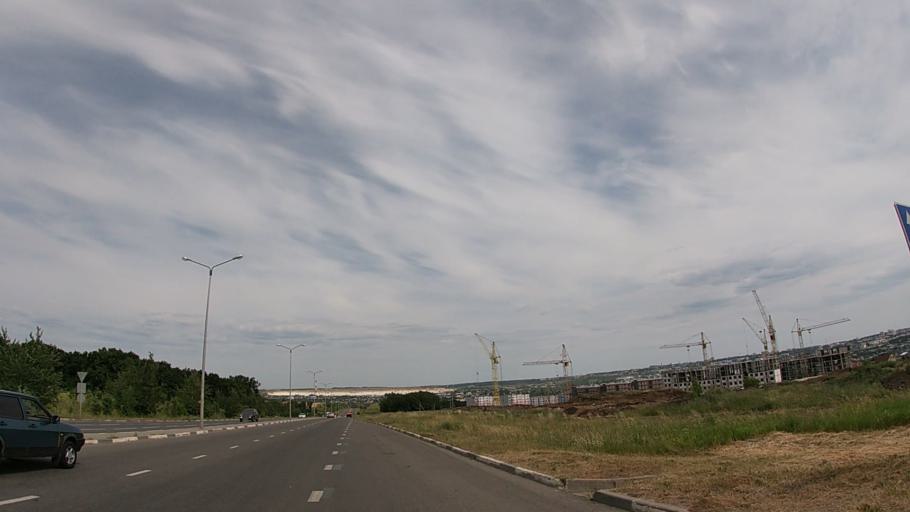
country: RU
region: Belgorod
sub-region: Belgorodskiy Rayon
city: Belgorod
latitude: 50.5944
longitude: 36.5310
